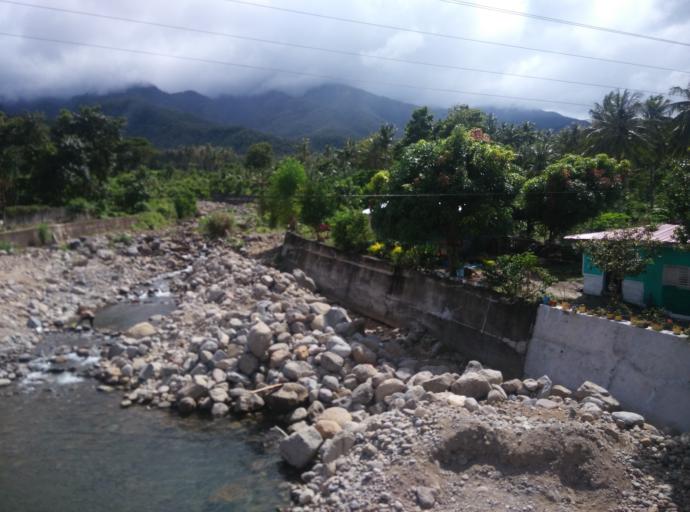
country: PH
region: Eastern Visayas
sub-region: Biliran
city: Tucdao
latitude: 11.7023
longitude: 124.4650
